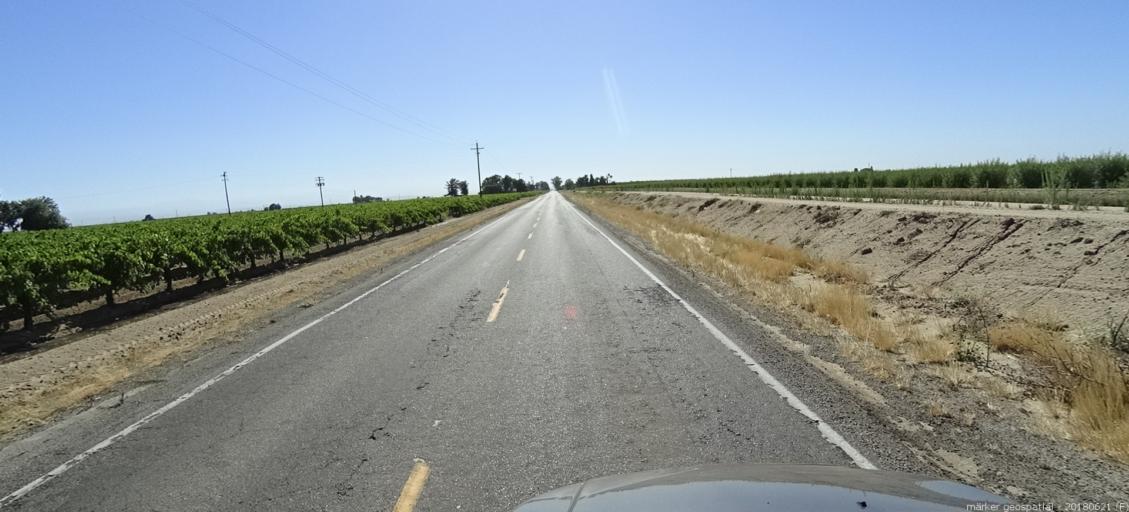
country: US
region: California
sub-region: Fresno County
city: Biola
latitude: 36.8513
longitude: -119.9965
